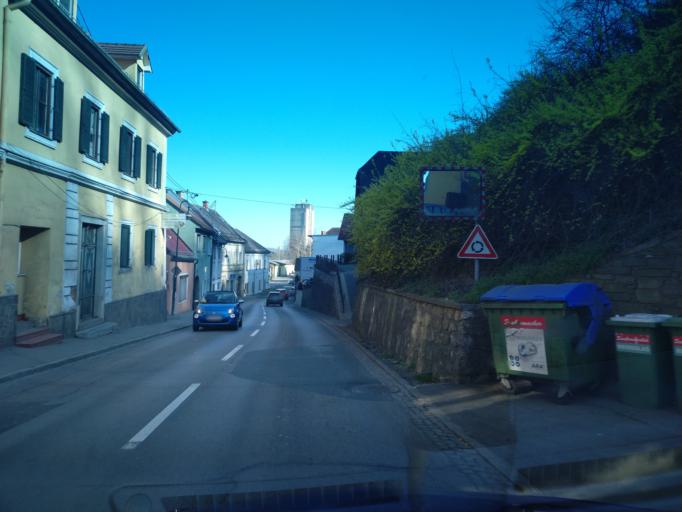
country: AT
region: Styria
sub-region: Politischer Bezirk Leibnitz
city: Wildon
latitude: 46.8864
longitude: 15.5170
